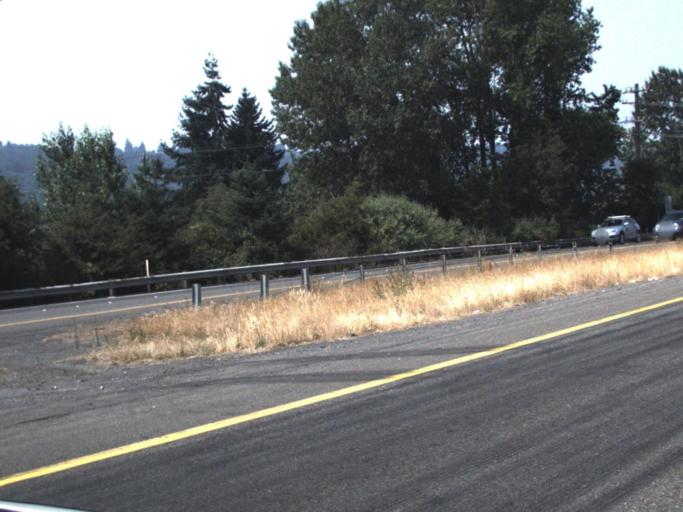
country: US
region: Washington
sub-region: King County
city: White Center
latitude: 47.5268
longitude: -122.3246
